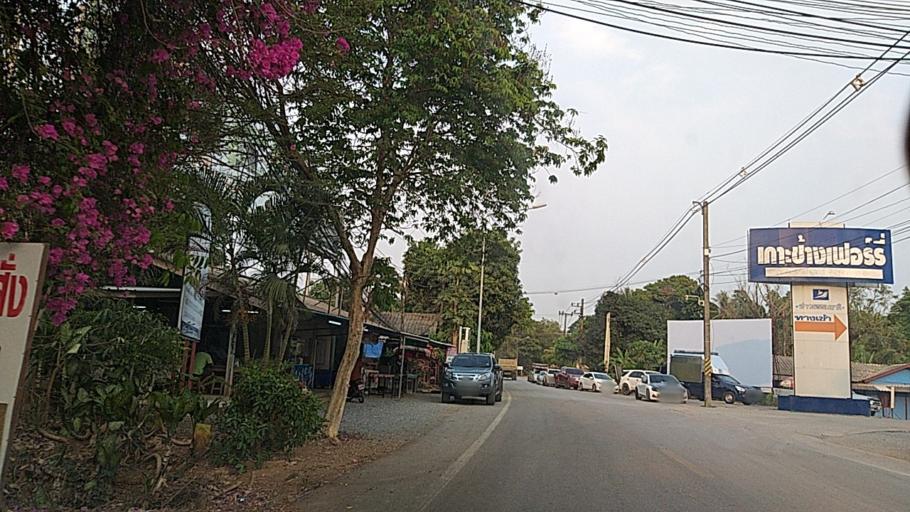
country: TH
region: Trat
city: Laem Ngop
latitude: 12.1894
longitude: 102.3009
